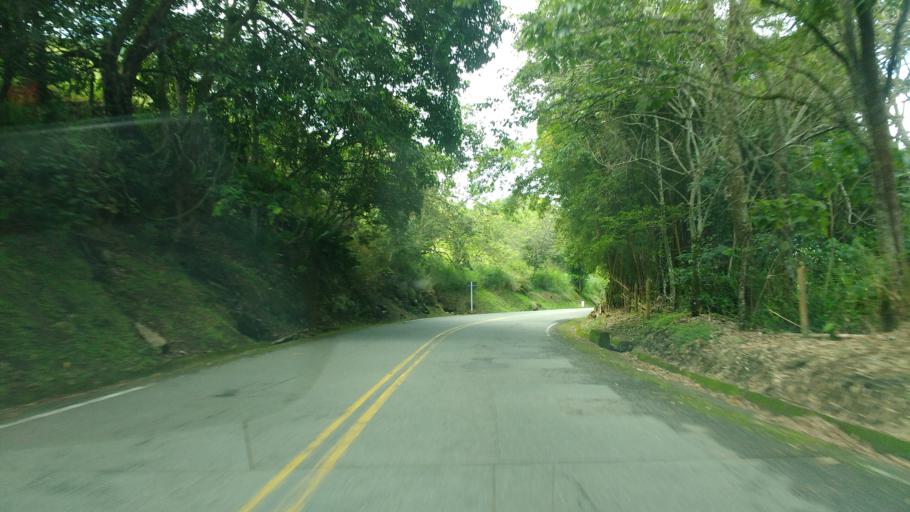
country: CO
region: Antioquia
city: Titiribi
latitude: 6.0361
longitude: -75.7623
